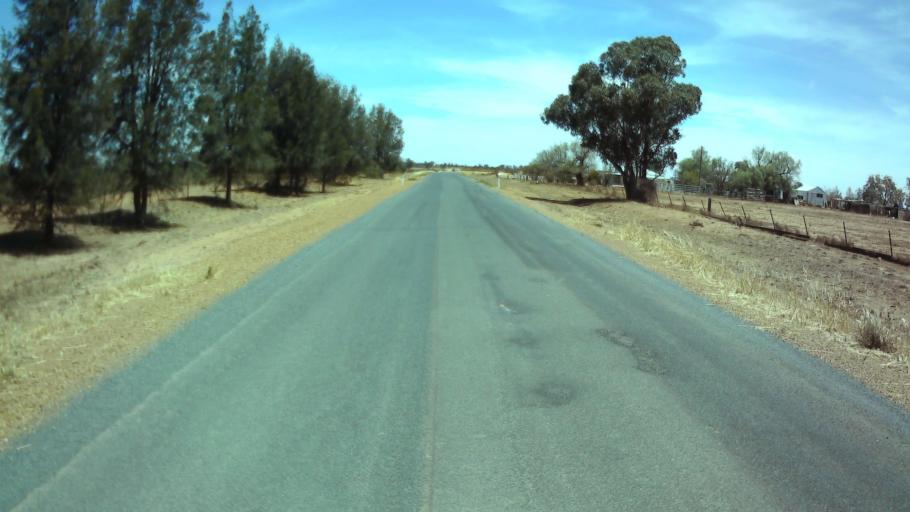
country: AU
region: New South Wales
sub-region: Weddin
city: Grenfell
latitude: -33.7489
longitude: 147.7675
